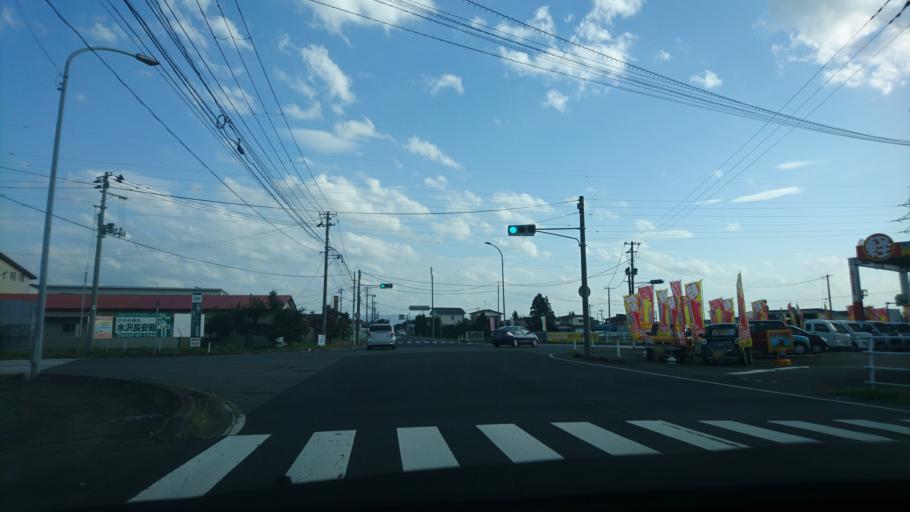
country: JP
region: Iwate
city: Mizusawa
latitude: 39.1590
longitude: 141.1803
